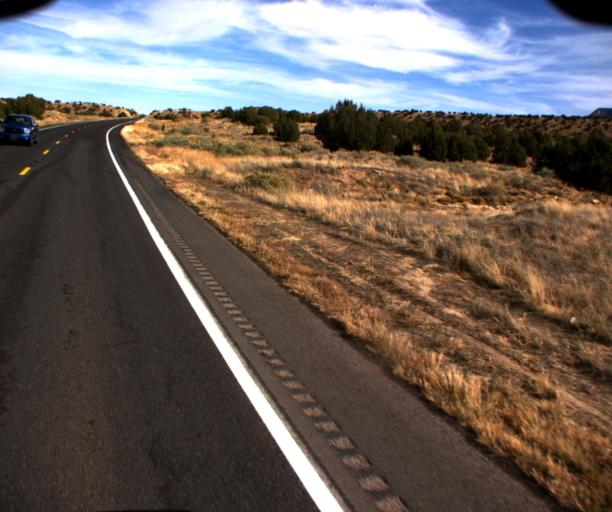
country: US
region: Arizona
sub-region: Navajo County
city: Kayenta
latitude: 36.6984
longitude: -110.3362
